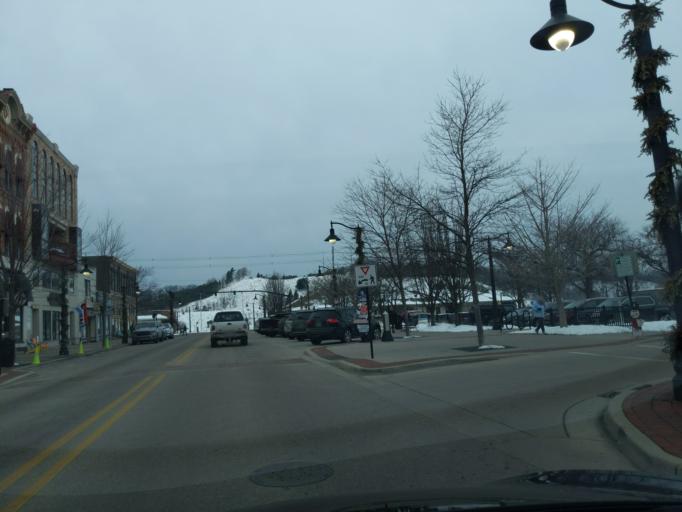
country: US
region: Michigan
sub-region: Ottawa County
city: Grand Haven
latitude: 43.0646
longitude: -86.2330
